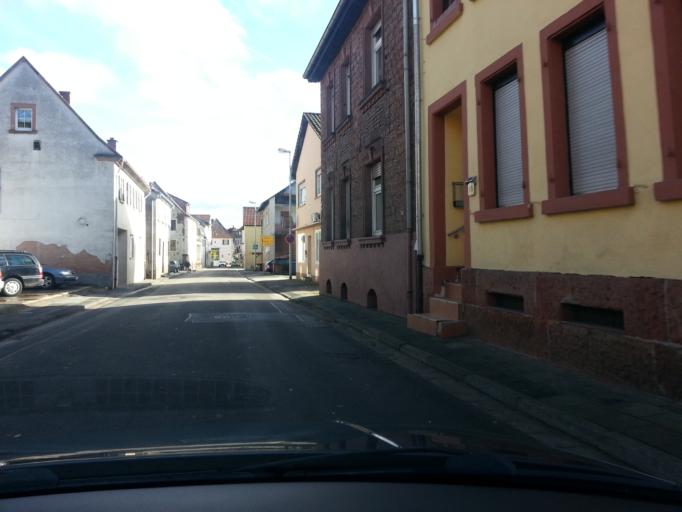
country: DE
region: Rheinland-Pfalz
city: Hochspeyer
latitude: 49.4435
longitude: 7.8934
